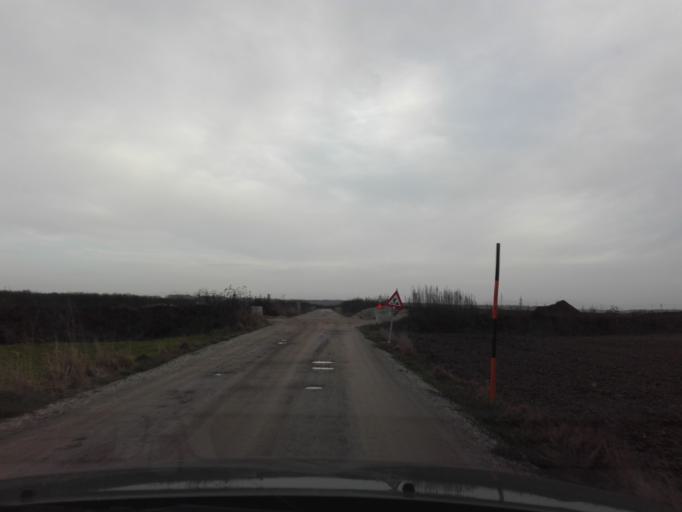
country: AT
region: Upper Austria
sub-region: Politischer Bezirk Linz-Land
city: Horsching
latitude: 48.2192
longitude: 14.1541
